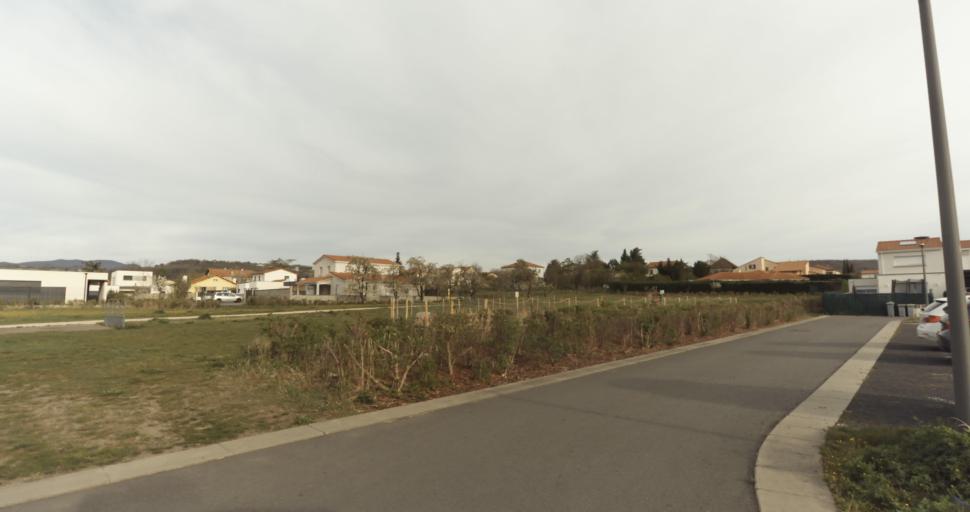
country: FR
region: Auvergne
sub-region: Departement du Puy-de-Dome
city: Cebazat
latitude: 45.8375
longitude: 3.1092
